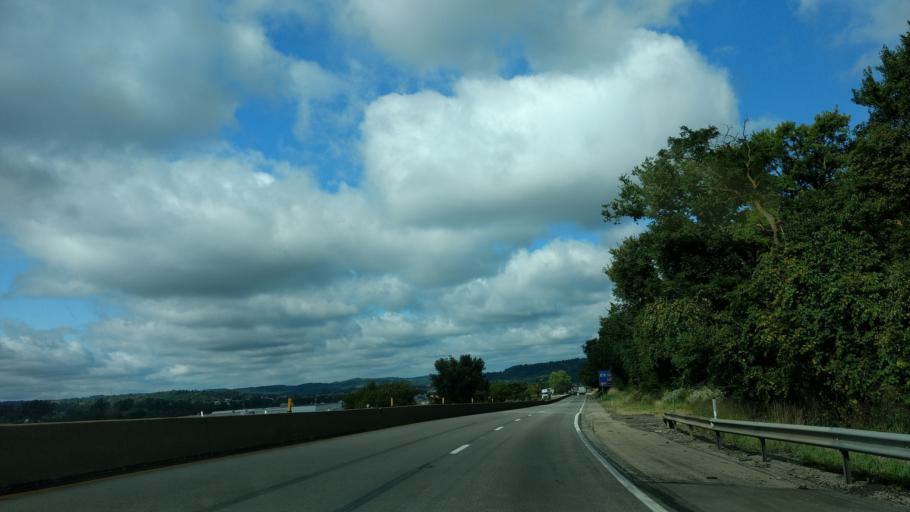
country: US
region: Pennsylvania
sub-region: Westmoreland County
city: Lynnwood-Pricedale
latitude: 40.1401
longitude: -79.8266
